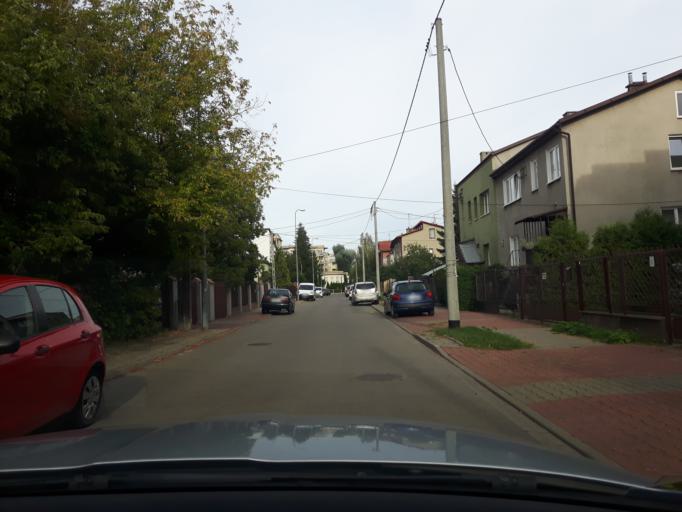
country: PL
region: Masovian Voivodeship
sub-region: Powiat wolominski
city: Zabki
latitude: 52.2835
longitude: 21.0788
